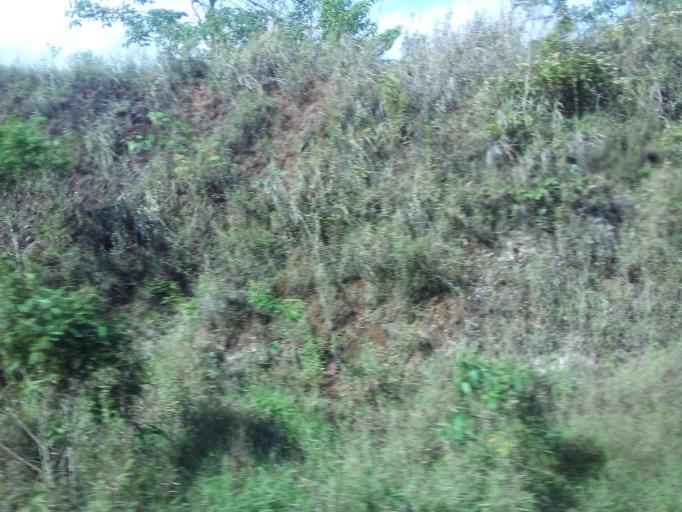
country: BR
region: Minas Gerais
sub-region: Caete
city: Caete
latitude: -19.8731
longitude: -43.7687
